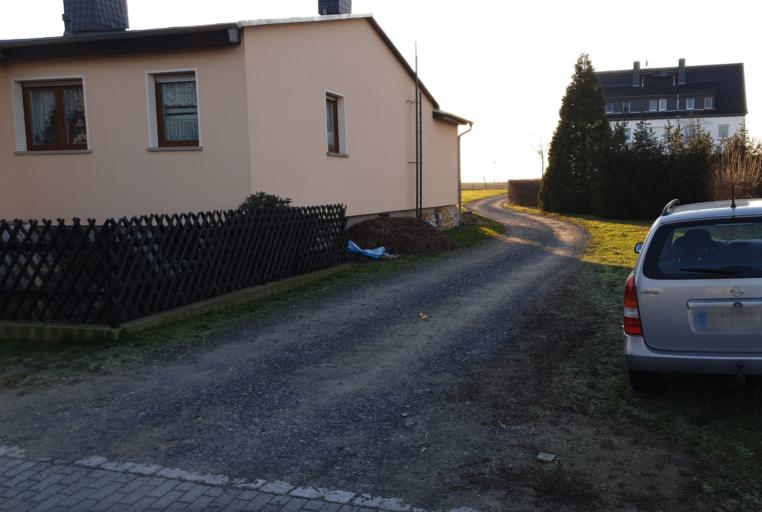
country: DE
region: Saxony
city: Mockrehna
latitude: 51.4764
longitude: 12.8519
